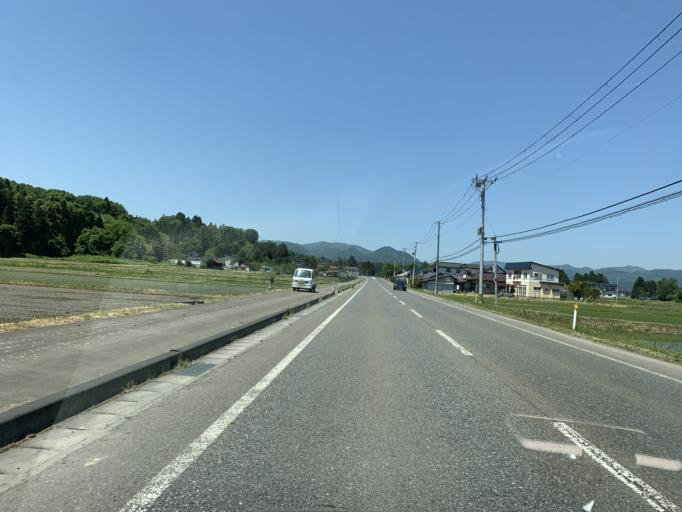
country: JP
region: Iwate
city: Kitakami
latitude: 39.2830
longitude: 141.0240
